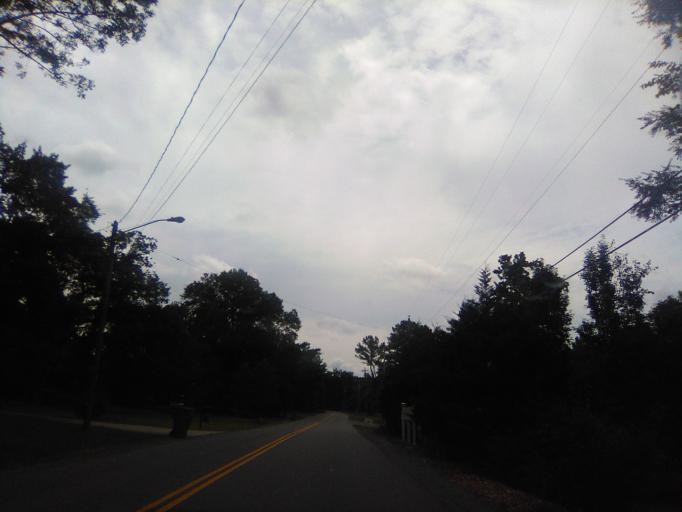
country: US
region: Tennessee
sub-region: Davidson County
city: Belle Meade
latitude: 36.1241
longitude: -86.8896
